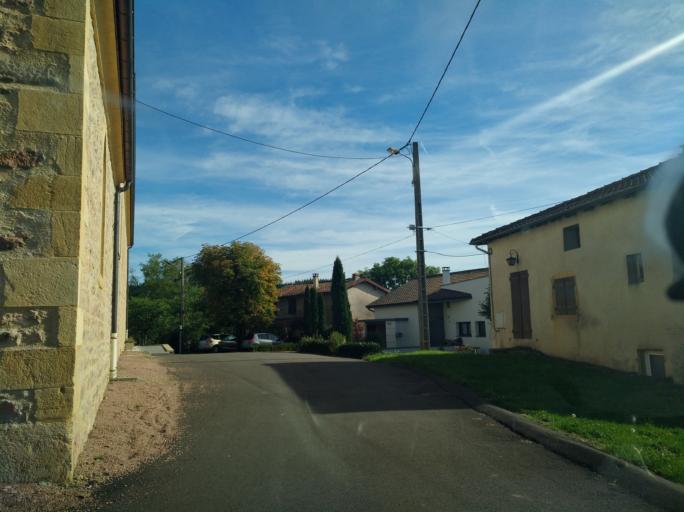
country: FR
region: Bourgogne
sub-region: Departement de Saone-et-Loire
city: Chauffailles
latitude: 46.2035
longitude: 4.3758
